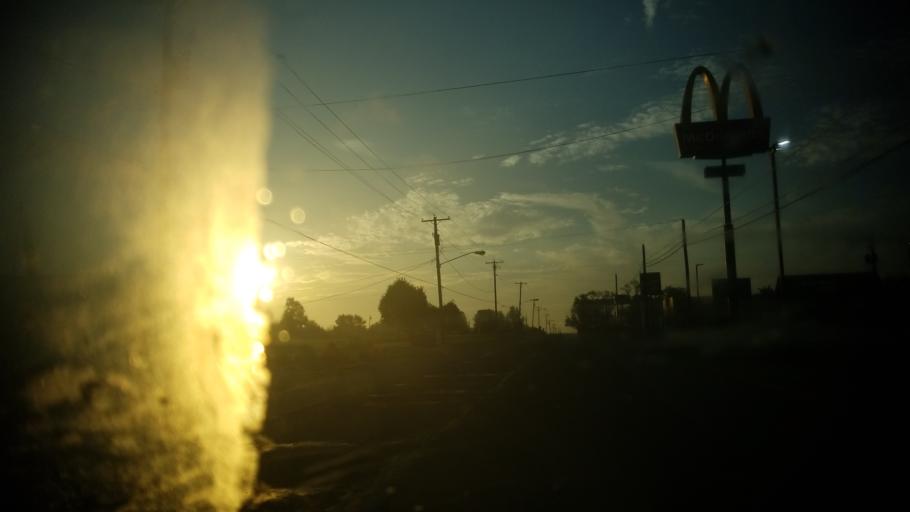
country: US
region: Illinois
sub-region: Wayne County
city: Fairfield
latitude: 38.3796
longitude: -88.3777
